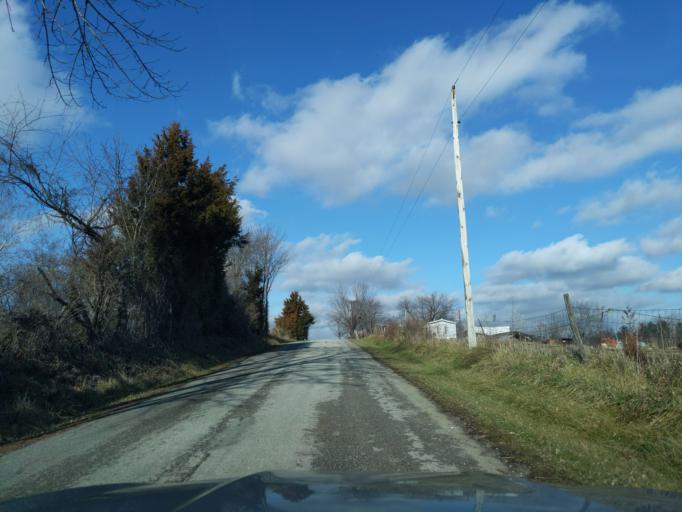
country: US
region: Indiana
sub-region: Decatur County
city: Greensburg
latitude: 39.2614
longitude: -85.4842
